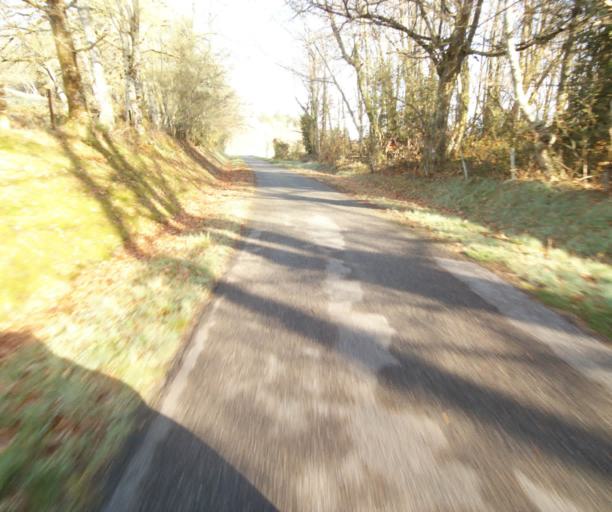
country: FR
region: Limousin
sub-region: Departement de la Correze
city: Correze
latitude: 45.2908
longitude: 1.8590
